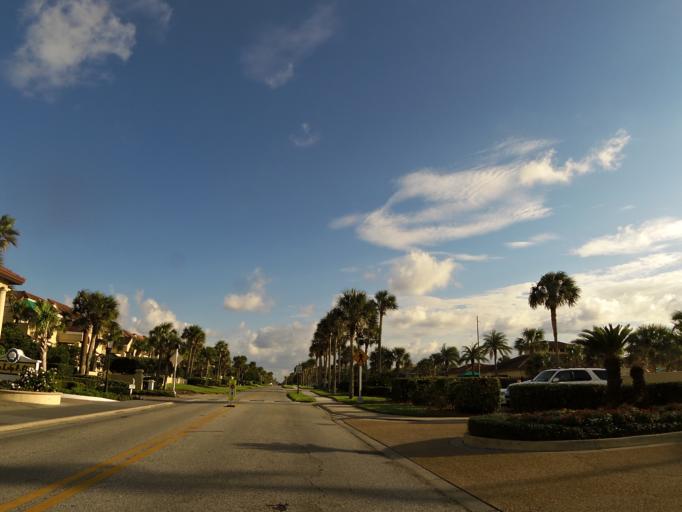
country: US
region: Florida
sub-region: Saint Johns County
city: Ponte Vedra Beach
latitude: 30.2184
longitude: -81.3721
